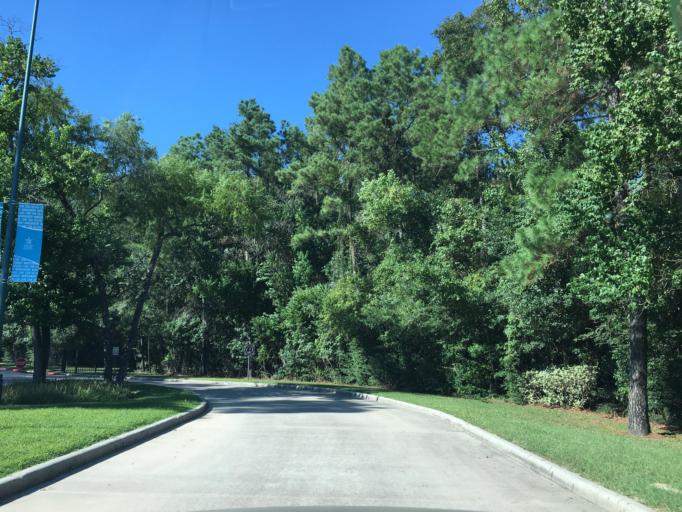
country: US
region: Texas
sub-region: Montgomery County
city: Shenandoah
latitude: 30.2077
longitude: -95.4639
